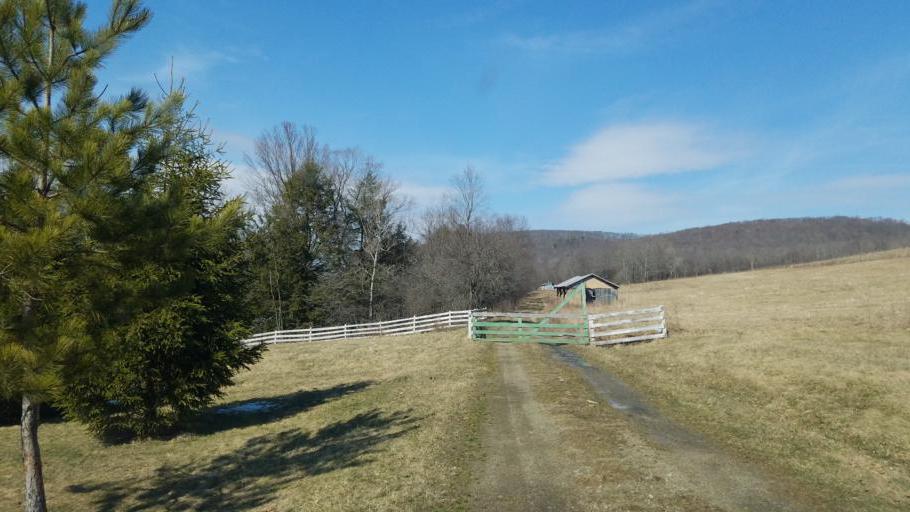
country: US
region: New York
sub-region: Allegany County
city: Andover
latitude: 41.9522
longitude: -77.8250
